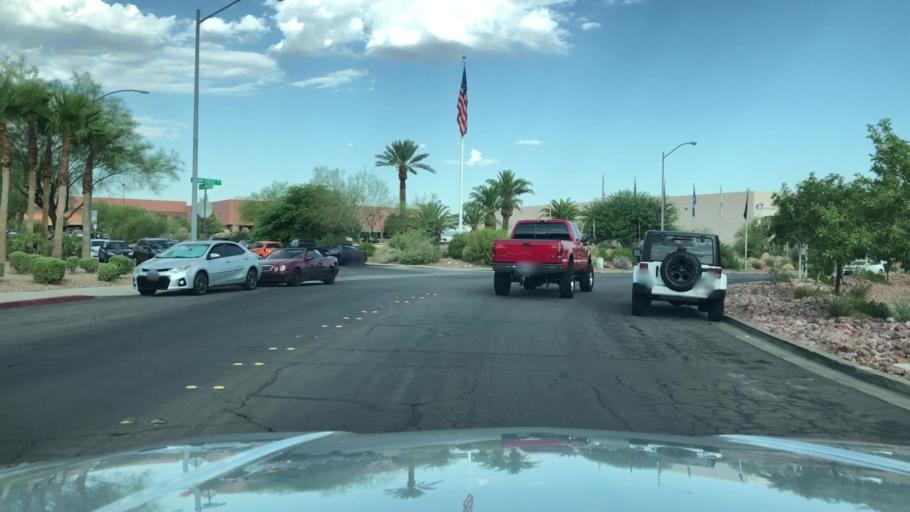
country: US
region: Nevada
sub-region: Clark County
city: Henderson
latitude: 36.0382
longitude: -115.0349
